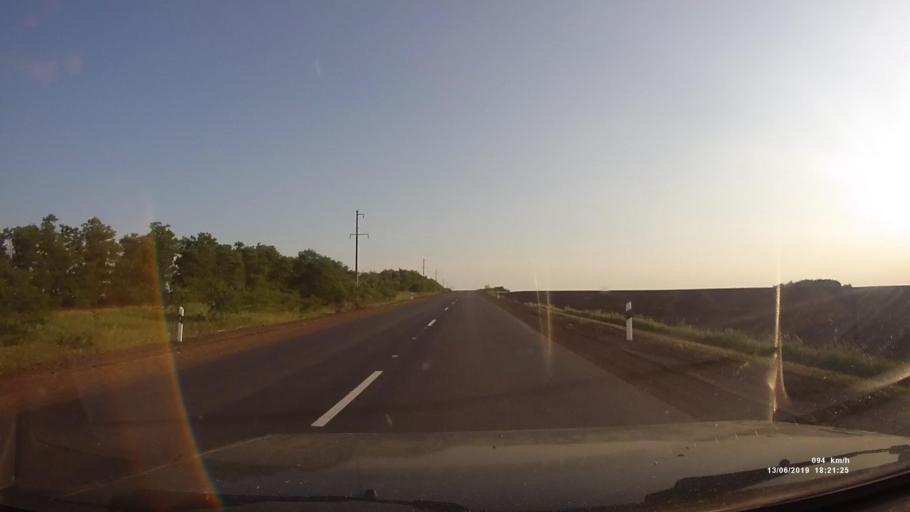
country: RU
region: Rostov
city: Kazanskaya
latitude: 49.8709
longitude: 41.2914
